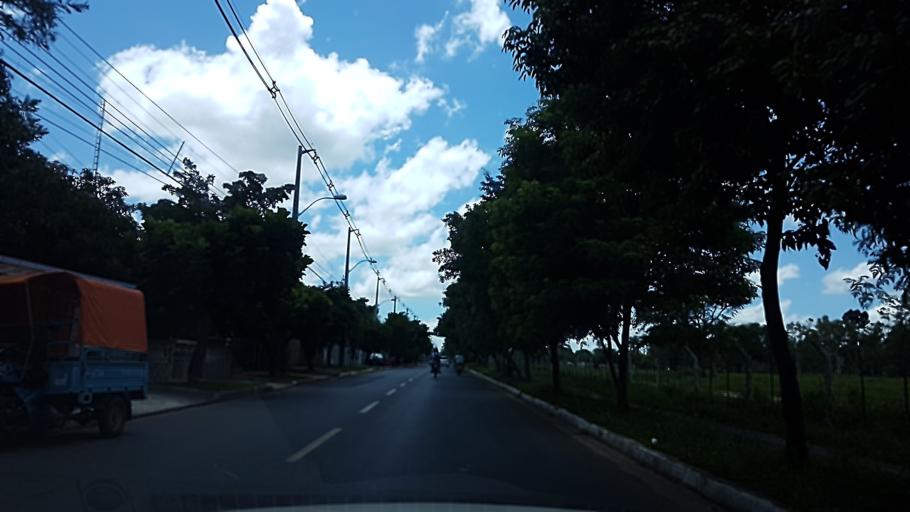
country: PY
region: Central
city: Colonia Mariano Roque Alonso
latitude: -25.2469
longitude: -57.5483
